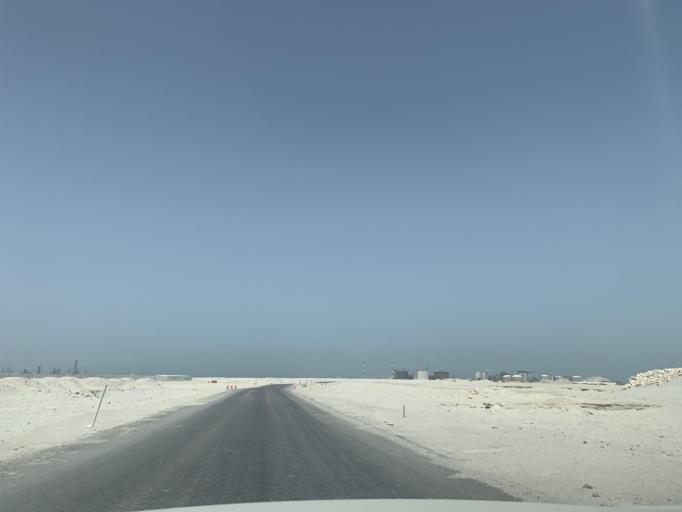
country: BH
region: Northern
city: Sitrah
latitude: 26.1570
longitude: 50.6368
